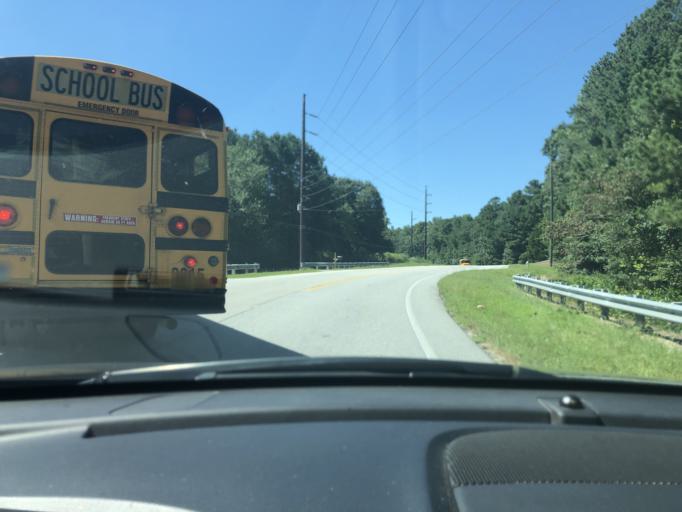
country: US
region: Georgia
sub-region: Gwinnett County
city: Grayson
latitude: 33.9212
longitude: -83.9467
